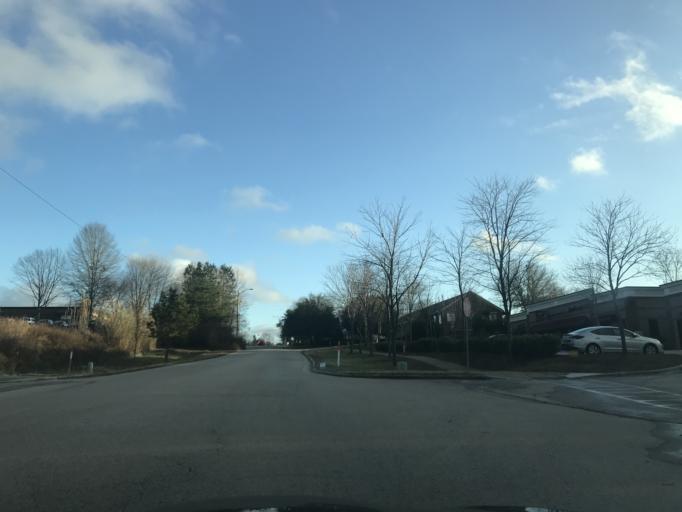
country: US
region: North Carolina
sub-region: Wake County
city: Wake Forest
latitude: 35.9514
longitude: -78.5323
